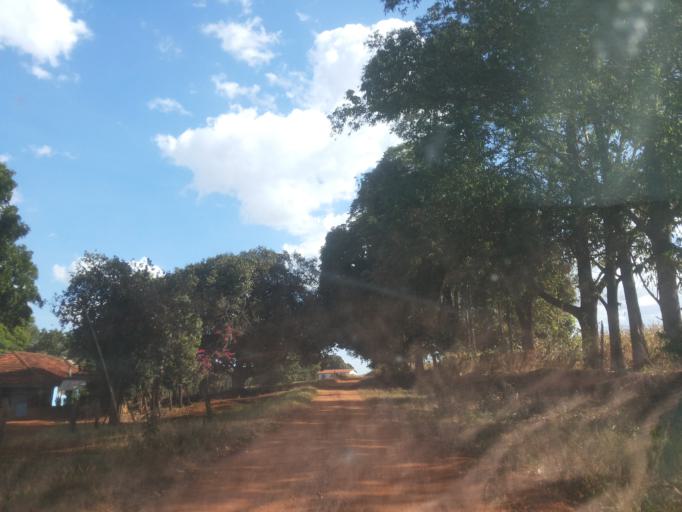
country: BR
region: Minas Gerais
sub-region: Capinopolis
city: Capinopolis
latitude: -18.5799
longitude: -49.4913
